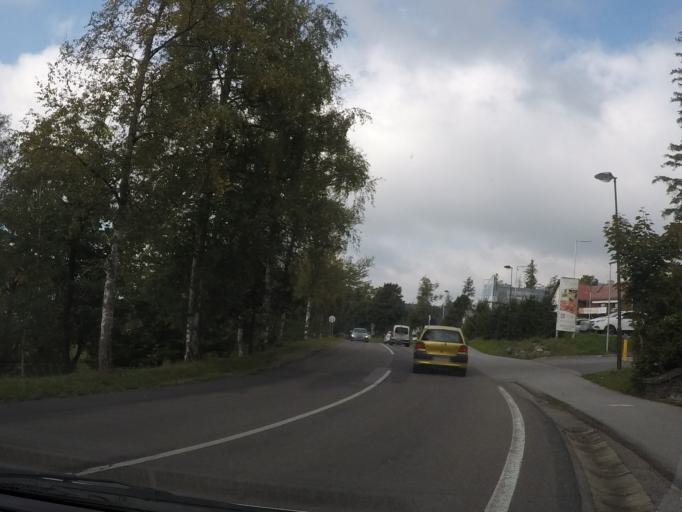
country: SK
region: Presovsky
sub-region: Okres Poprad
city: Vysoke Tatry
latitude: 49.1373
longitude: 20.2154
